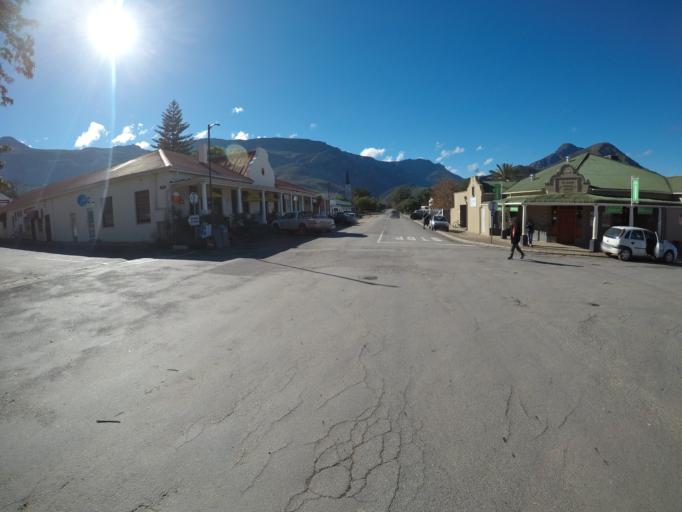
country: ZA
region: Western Cape
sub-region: Overberg District Municipality
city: Caledon
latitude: -34.0498
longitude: 19.6084
